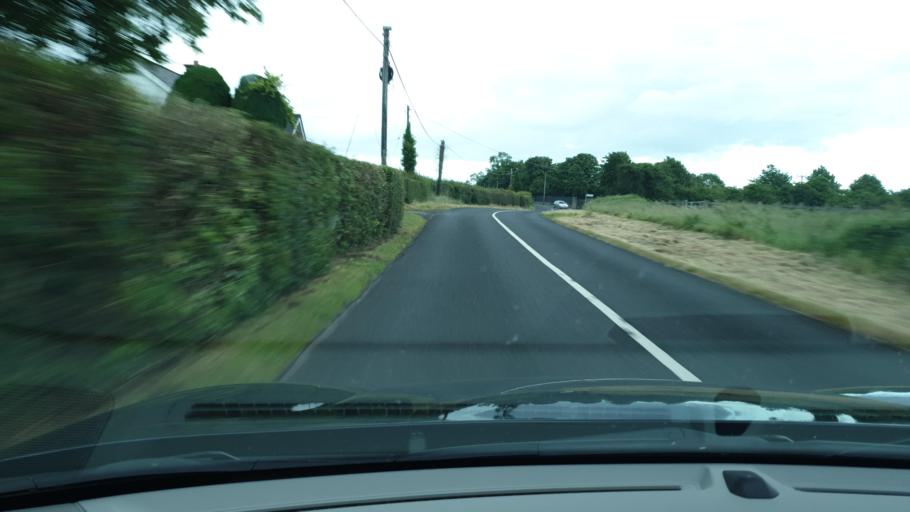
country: IE
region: Leinster
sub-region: An Mhi
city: Navan
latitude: 53.6433
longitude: -6.7224
